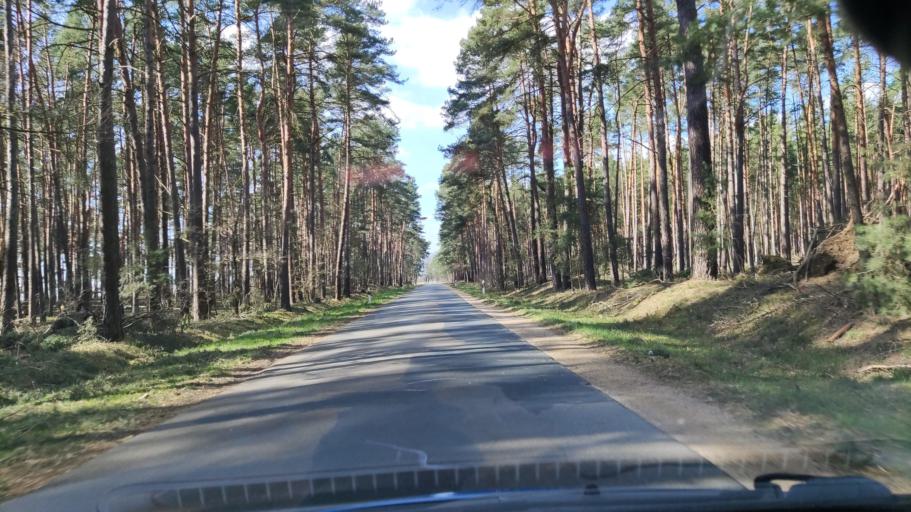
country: DE
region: Lower Saxony
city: Trebel
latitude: 53.0019
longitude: 11.2858
